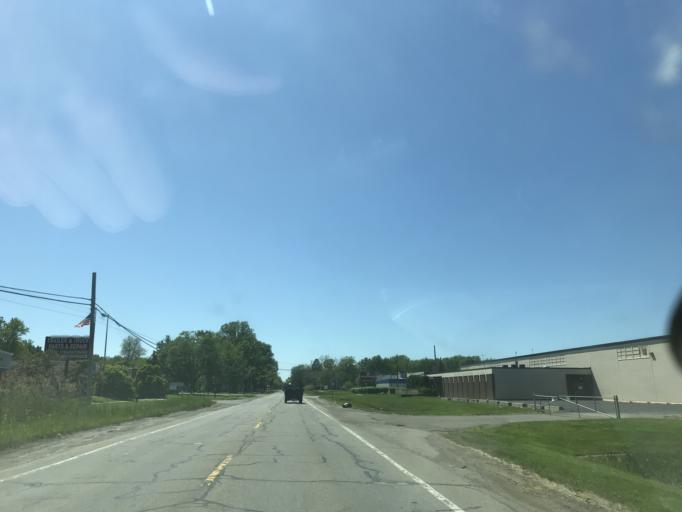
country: US
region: Michigan
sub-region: Wayne County
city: Inkster
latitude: 42.2531
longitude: -83.3369
